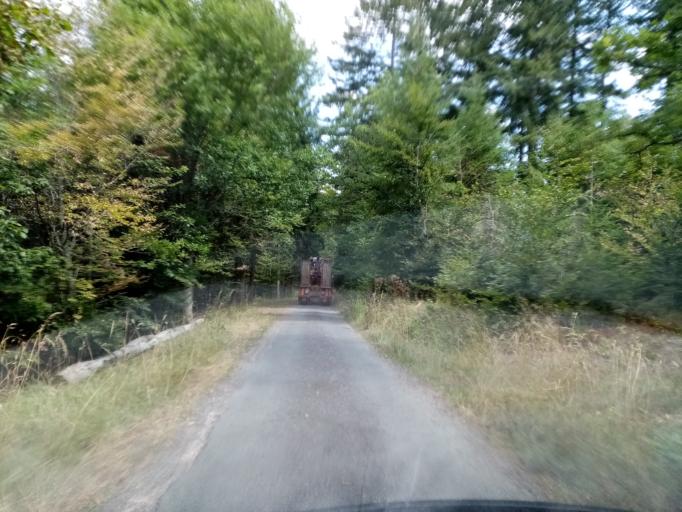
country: FR
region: Alsace
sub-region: Departement du Bas-Rhin
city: Dambach-la-Ville
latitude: 48.3440
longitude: 7.3892
